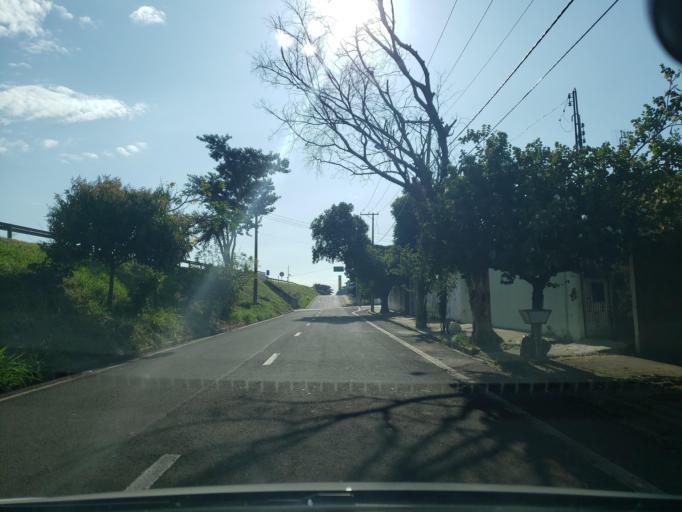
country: BR
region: Sao Paulo
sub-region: Aracatuba
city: Aracatuba
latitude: -21.2146
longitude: -50.4645
